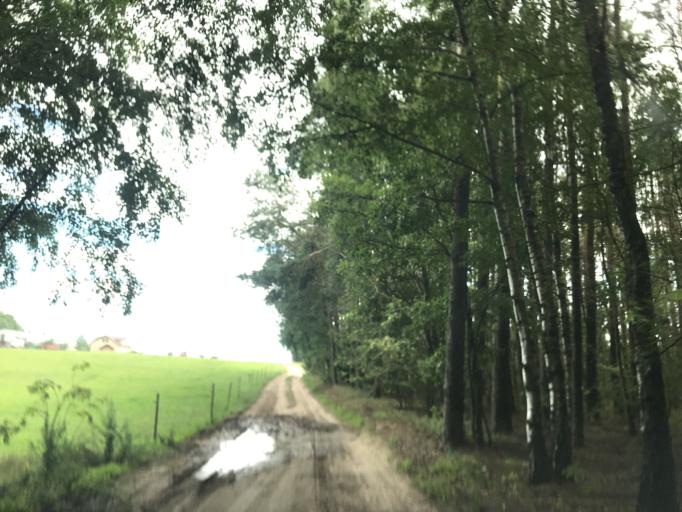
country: PL
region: Kujawsko-Pomorskie
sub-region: Powiat brodnicki
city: Brzozie
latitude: 53.3235
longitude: 19.6883
